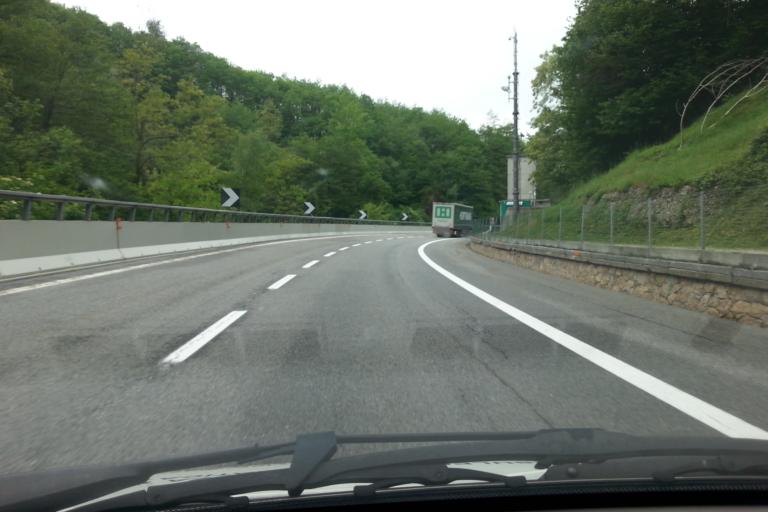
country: IT
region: Piedmont
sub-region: Provincia di Cuneo
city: Castelnuovo di Ceva
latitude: 44.3641
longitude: 8.1336
